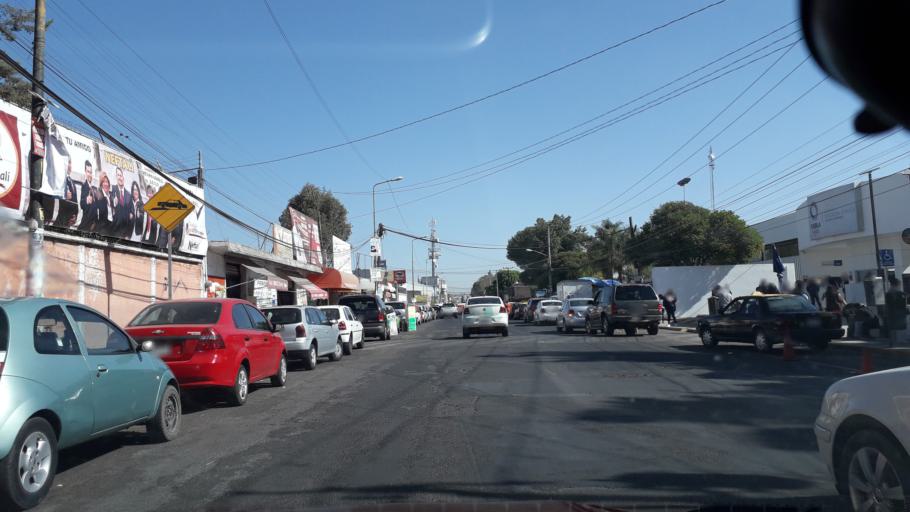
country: MX
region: Puebla
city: Puebla
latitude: 19.0739
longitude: -98.2111
